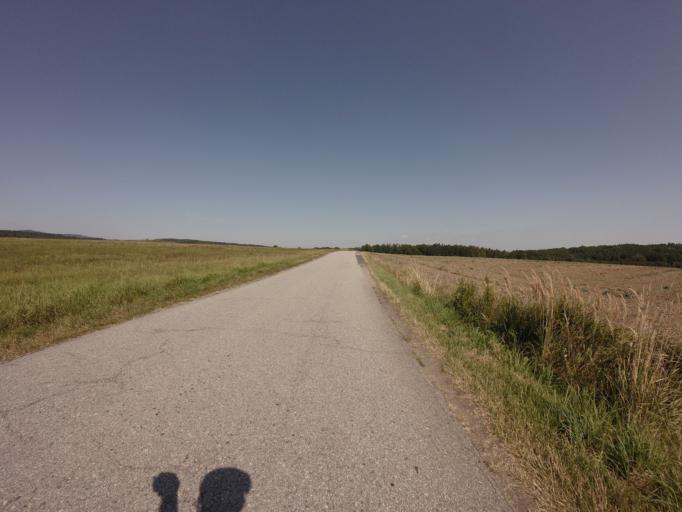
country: CZ
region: Jihocesky
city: Kamenny Ujezd
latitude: 48.9073
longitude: 14.4353
